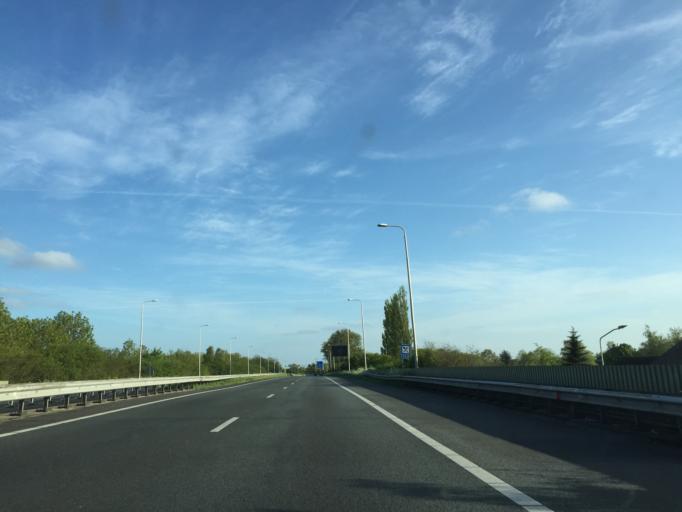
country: NL
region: North Holland
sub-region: Gemeente Hoorn
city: Hoorn
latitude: 52.6815
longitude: 5.0304
